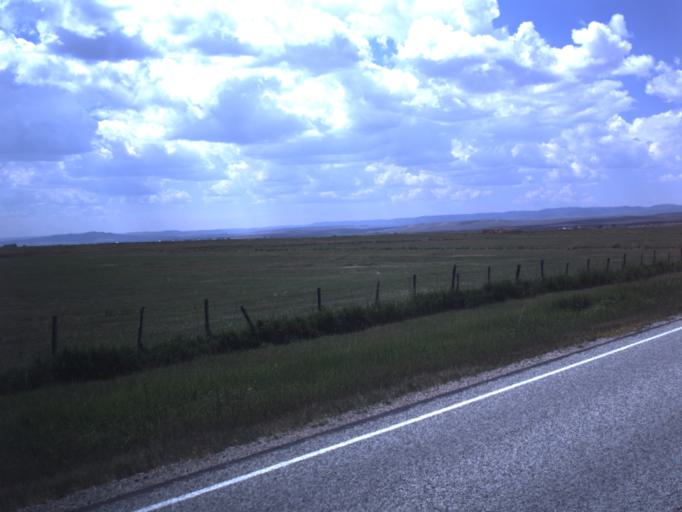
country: US
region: Utah
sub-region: Rich County
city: Randolph
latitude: 41.7753
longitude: -111.0931
